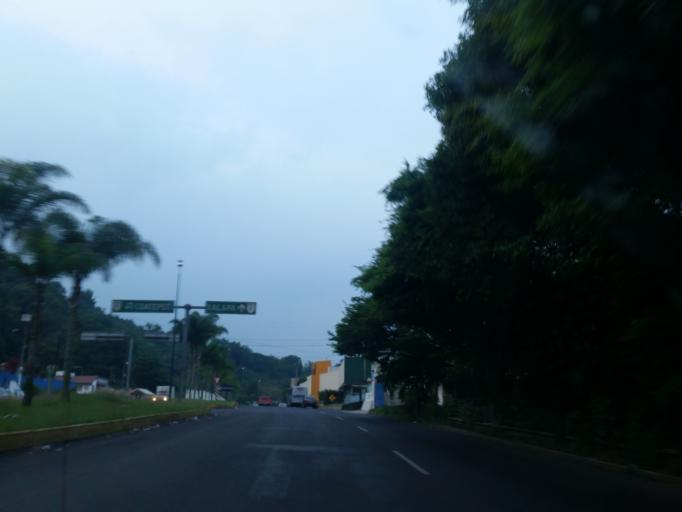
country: MX
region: Veracruz
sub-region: Xalapa
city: Xalapa de Enriquez
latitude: 19.5012
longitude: -96.9361
